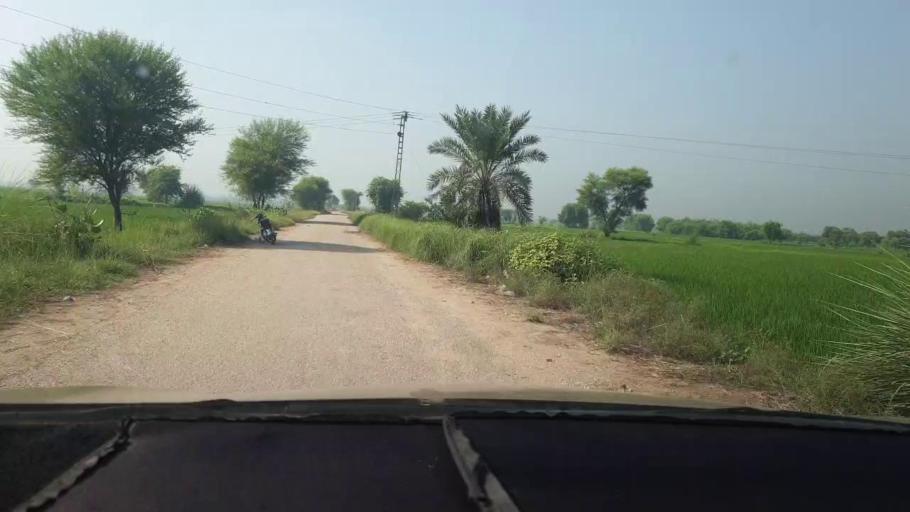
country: PK
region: Sindh
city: Kambar
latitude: 27.6327
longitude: 68.0899
